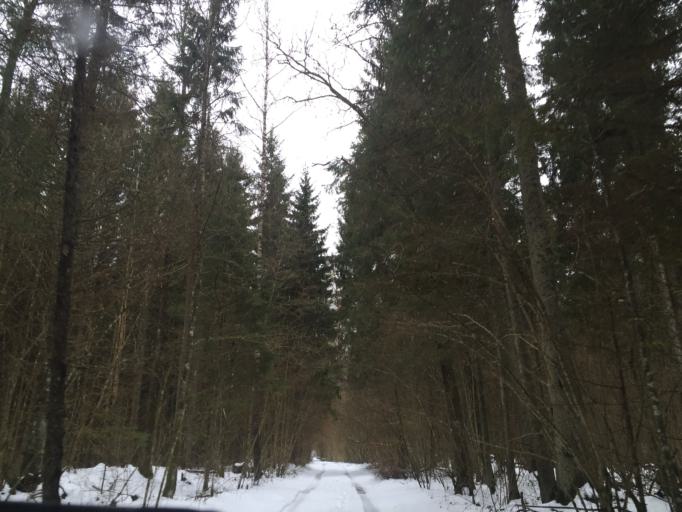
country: LV
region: Krimulda
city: Ragana
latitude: 57.1358
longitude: 24.7239
